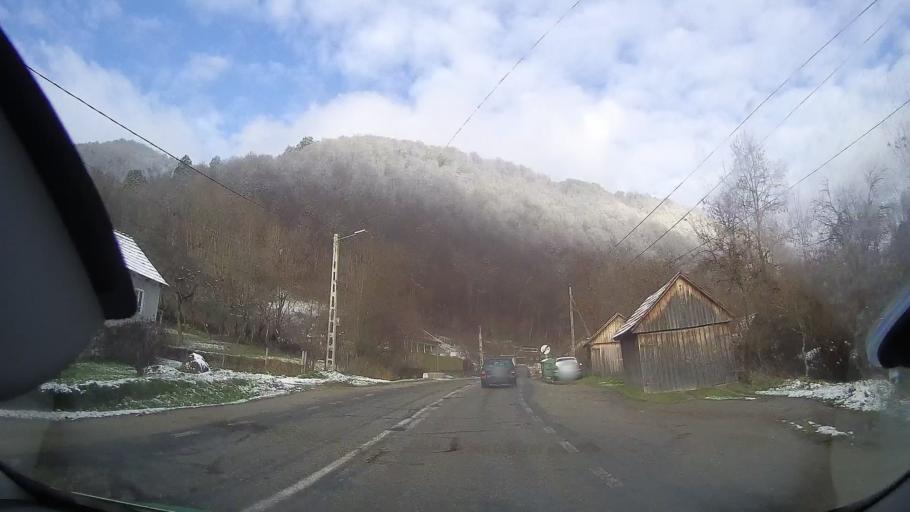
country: RO
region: Alba
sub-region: Oras Baia de Aries
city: Baia de Aries
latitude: 46.3860
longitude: 23.2804
